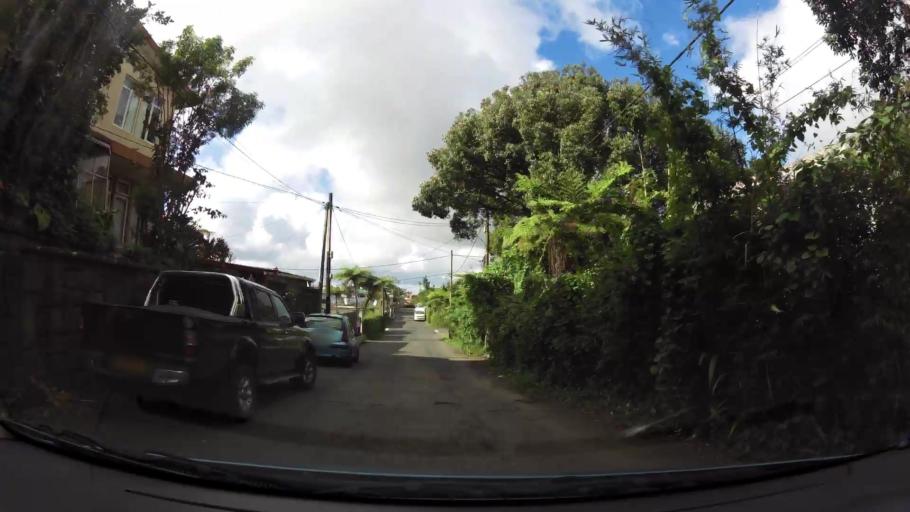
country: MU
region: Plaines Wilhems
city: Curepipe
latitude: -20.3287
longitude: 57.5196
